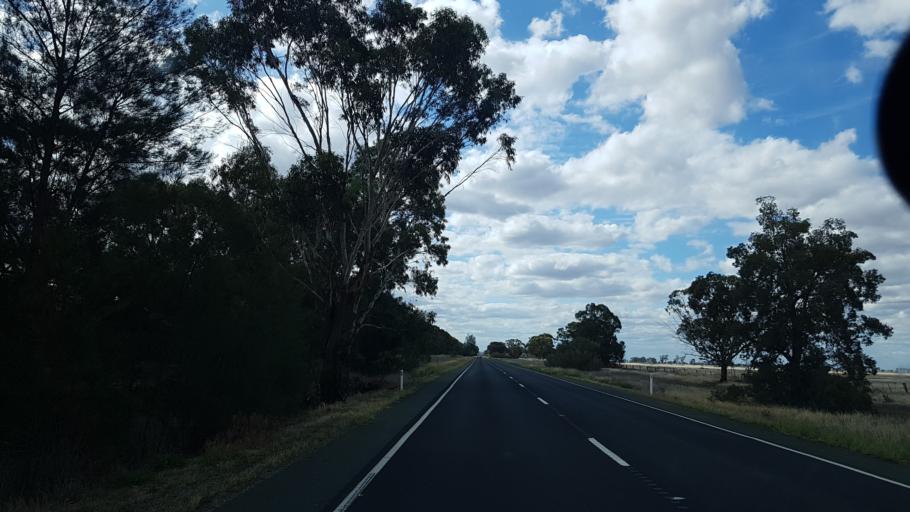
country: AU
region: Victoria
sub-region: Swan Hill
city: Swan Hill
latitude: -35.9859
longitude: 143.9456
